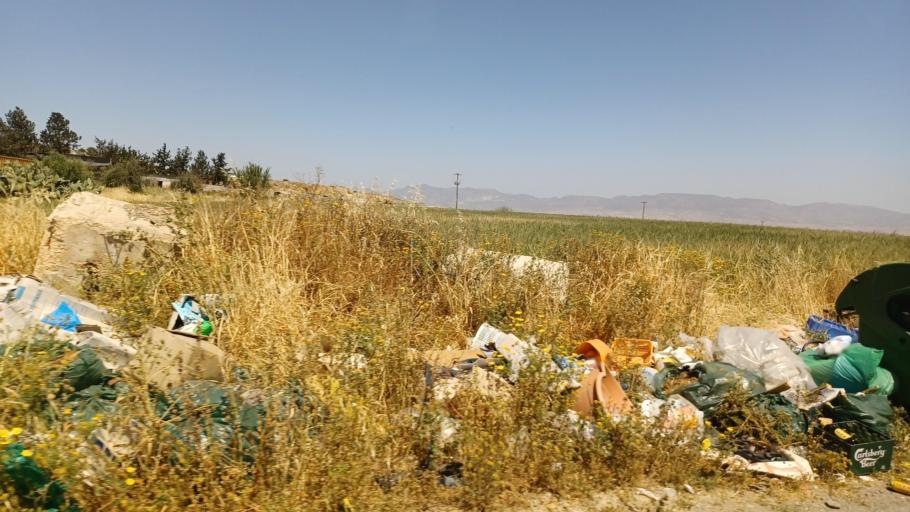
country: CY
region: Lefkosia
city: Kokkinotrimithia
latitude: 35.1513
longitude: 33.2419
